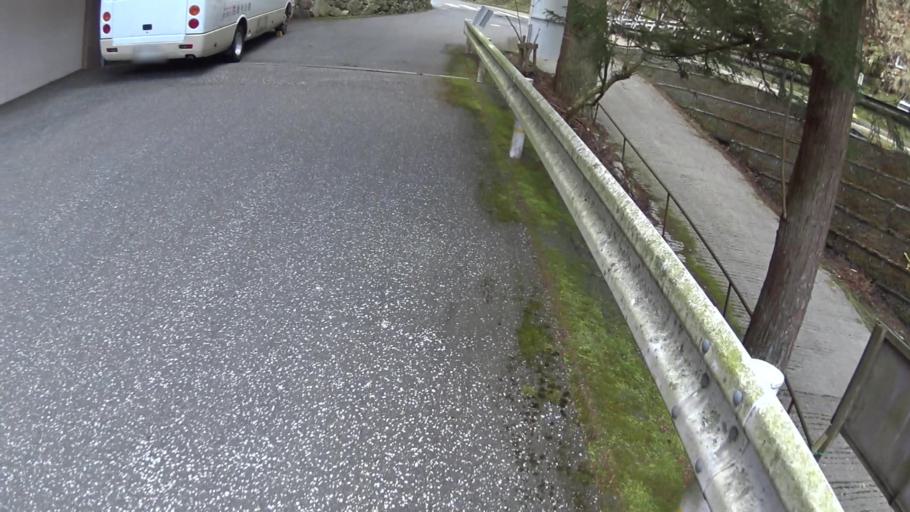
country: JP
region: Shiga Prefecture
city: Otsu-shi
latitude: 35.0686
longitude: 135.8418
